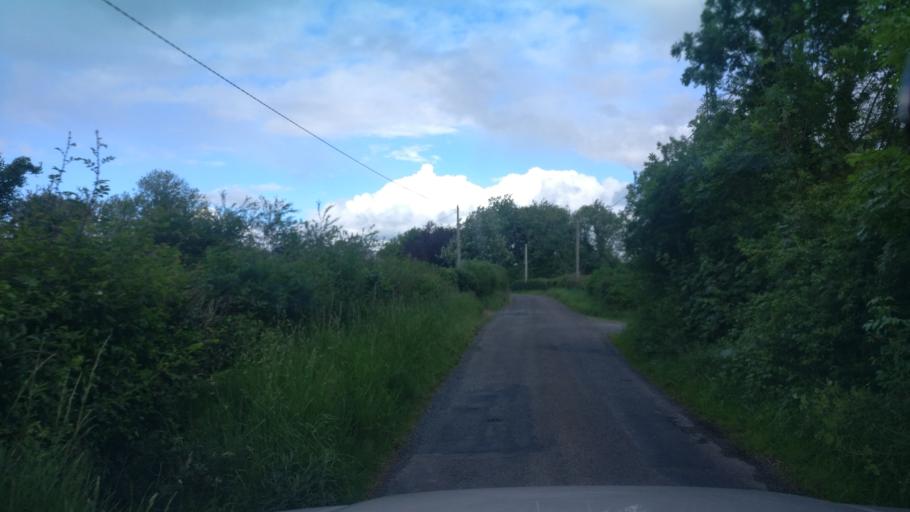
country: IE
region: Connaught
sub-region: County Galway
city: Portumna
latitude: 53.1988
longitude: -8.3527
